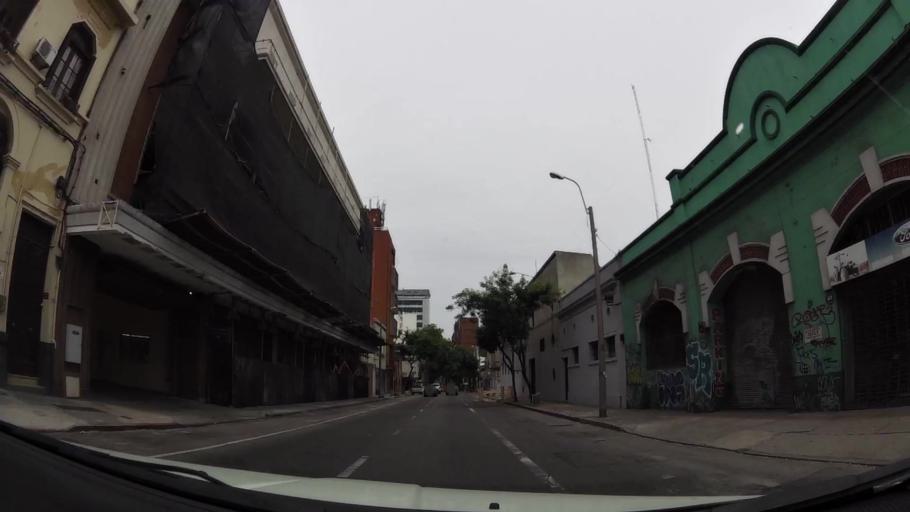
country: UY
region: Montevideo
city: Montevideo
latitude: -34.8993
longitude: -56.1723
